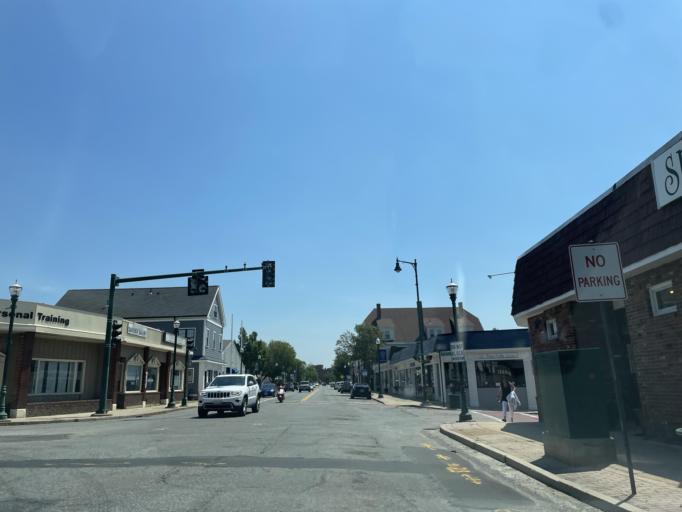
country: US
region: Massachusetts
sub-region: Norfolk County
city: Braintree
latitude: 42.2210
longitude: -71.0042
